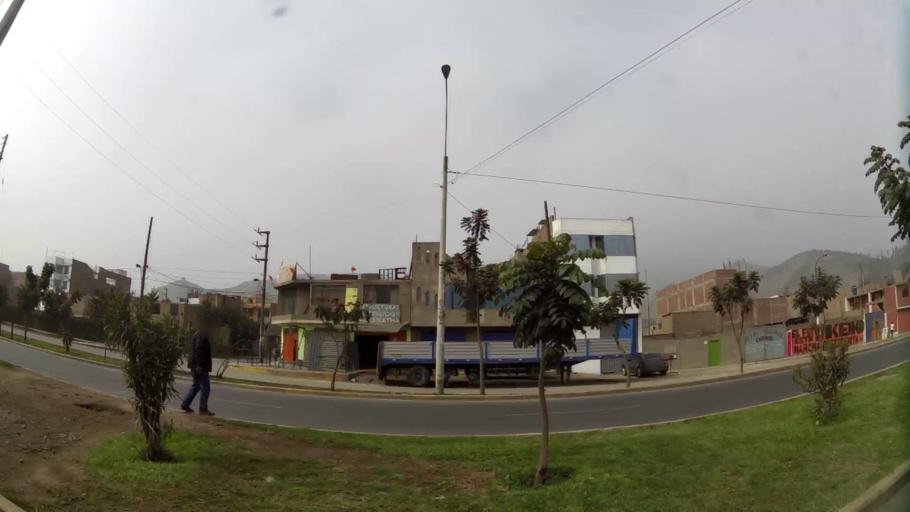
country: PE
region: Lima
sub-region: Lima
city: Santa Maria
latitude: -12.0007
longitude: -76.8333
